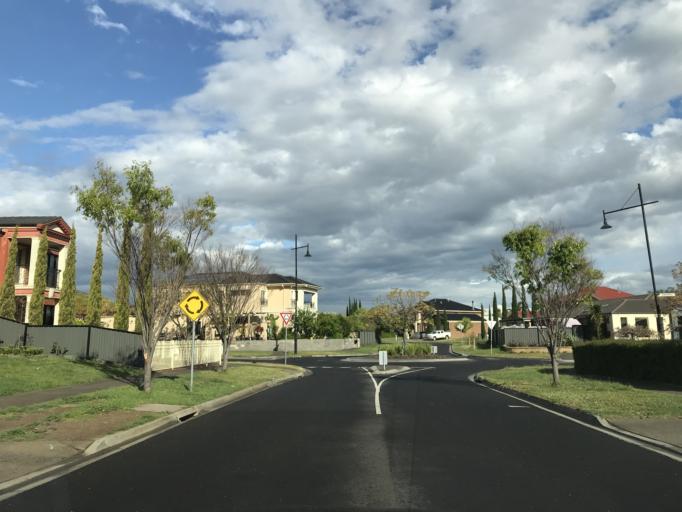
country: AU
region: Victoria
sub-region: Brimbank
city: Derrimut
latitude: -37.7908
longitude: 144.7675
